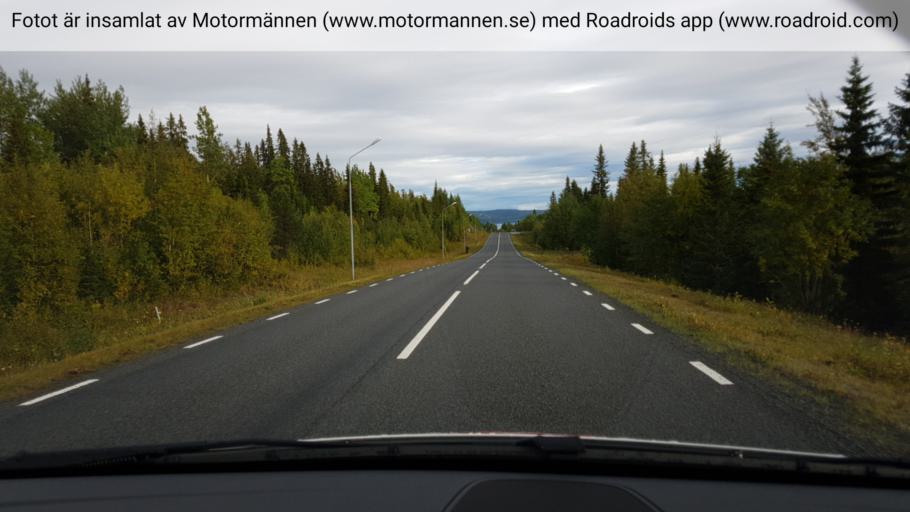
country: SE
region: Jaemtland
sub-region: Are Kommun
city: Are
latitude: 63.4781
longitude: 13.2086
